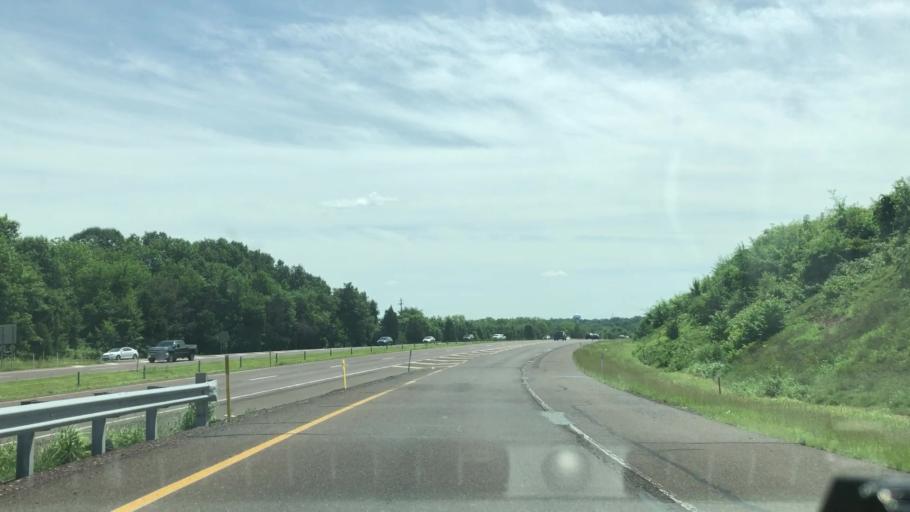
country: US
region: Pennsylvania
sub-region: Montgomery County
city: Royersford
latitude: 40.1938
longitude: -75.5235
